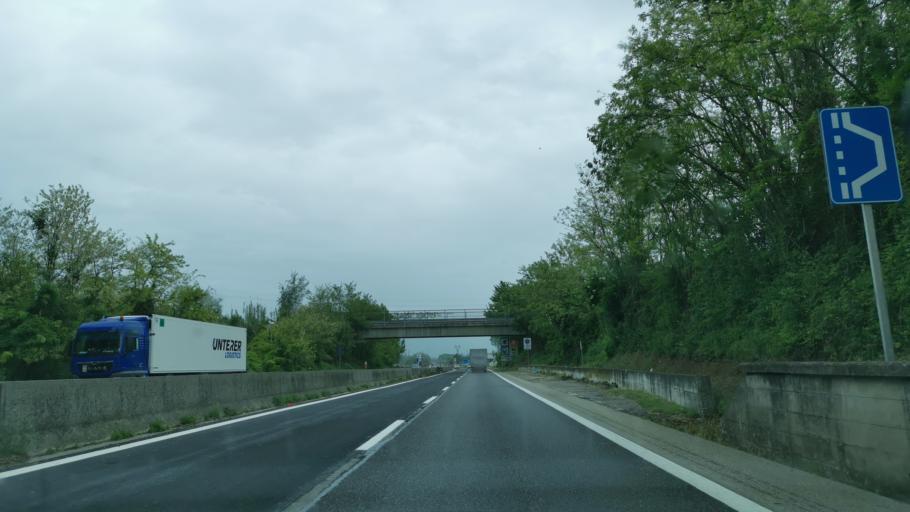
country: IT
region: Veneto
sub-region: Provincia di Verona
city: Cola
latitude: 45.4752
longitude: 10.7631
